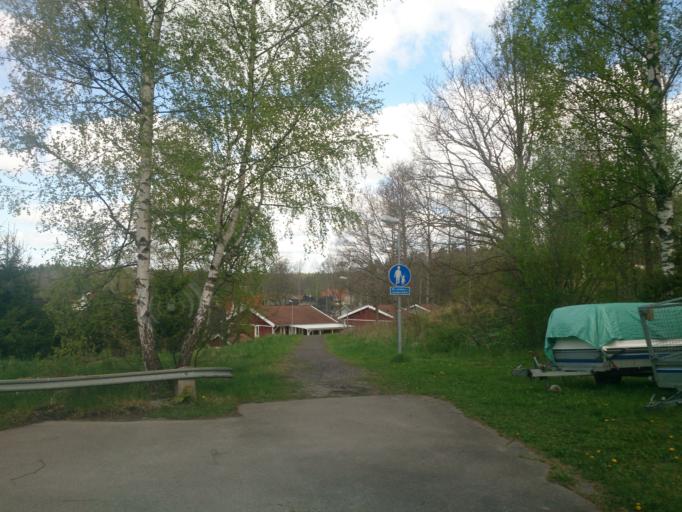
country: SE
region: OEstergoetland
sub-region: Atvidabergs Kommun
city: Atvidaberg
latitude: 58.2020
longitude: 15.9753
